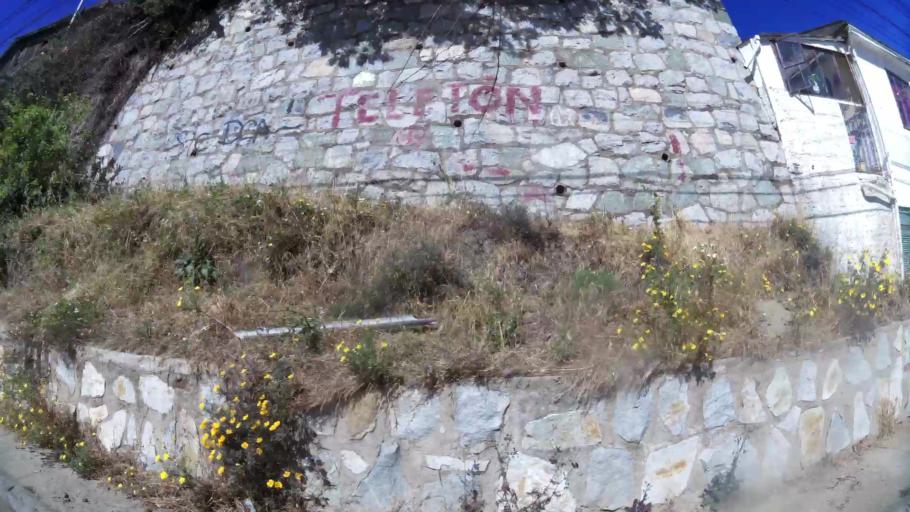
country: CL
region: Valparaiso
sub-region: Provincia de Valparaiso
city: Vina del Mar
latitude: -33.0331
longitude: -71.5724
